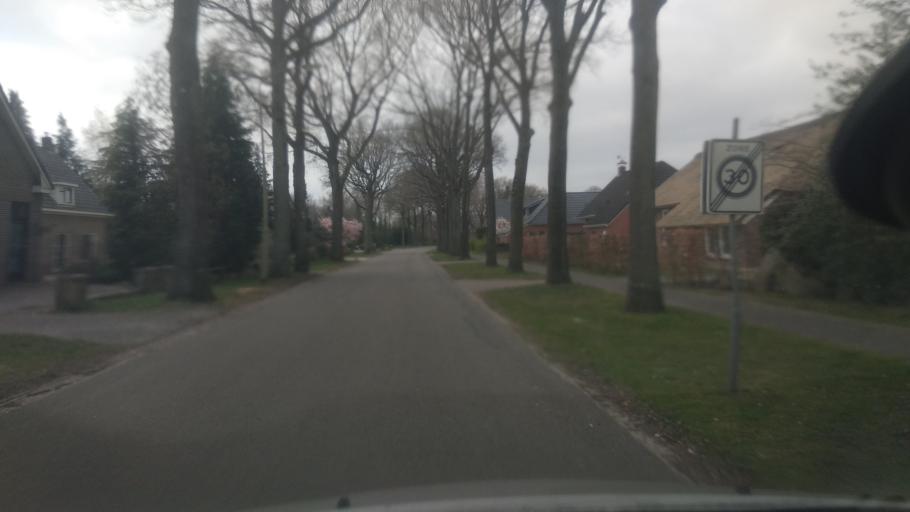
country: NL
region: Drenthe
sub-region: Gemeente Emmen
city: Emmen
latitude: 52.8428
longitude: 6.8907
